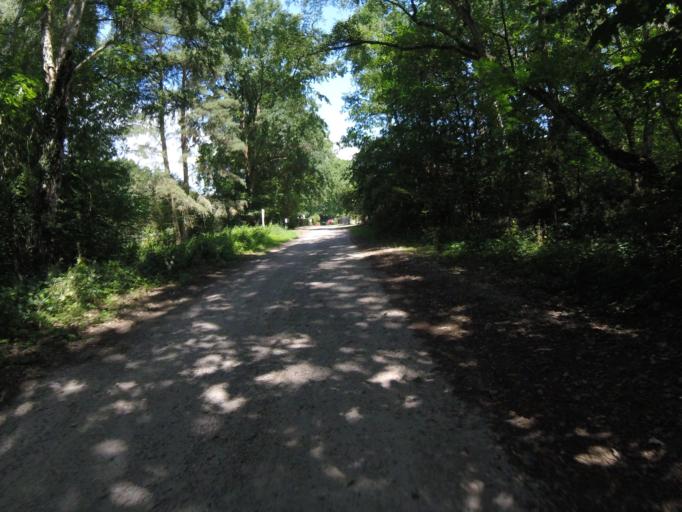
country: DE
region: Brandenburg
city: Bestensee
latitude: 52.2208
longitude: 13.6520
